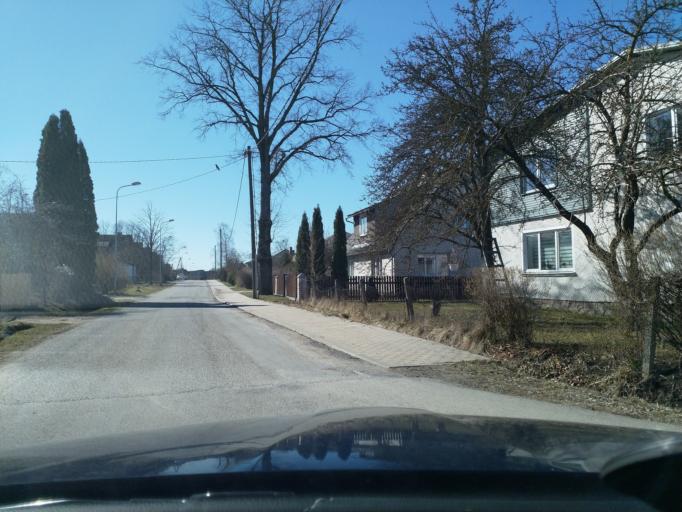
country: LV
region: Kuldigas Rajons
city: Kuldiga
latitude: 56.9664
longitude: 21.9952
